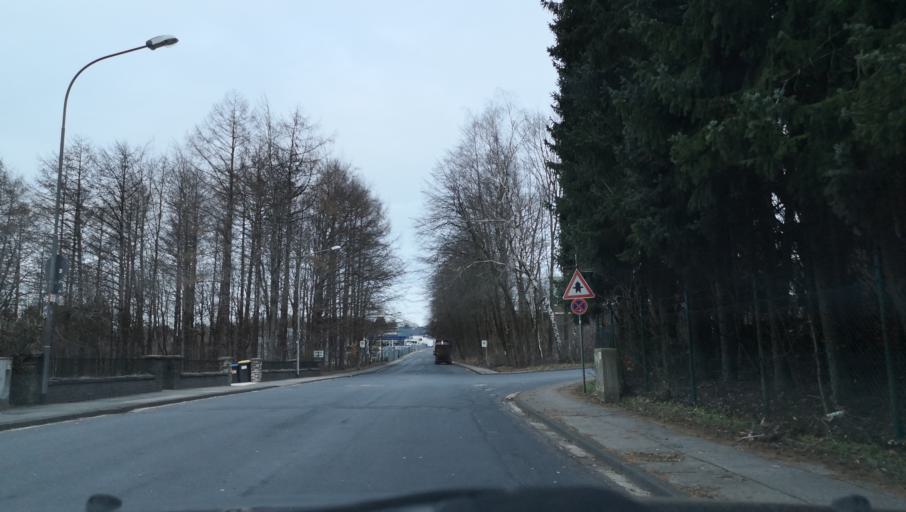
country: DE
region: North Rhine-Westphalia
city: Wermelskirchen
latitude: 51.1771
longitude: 7.2440
